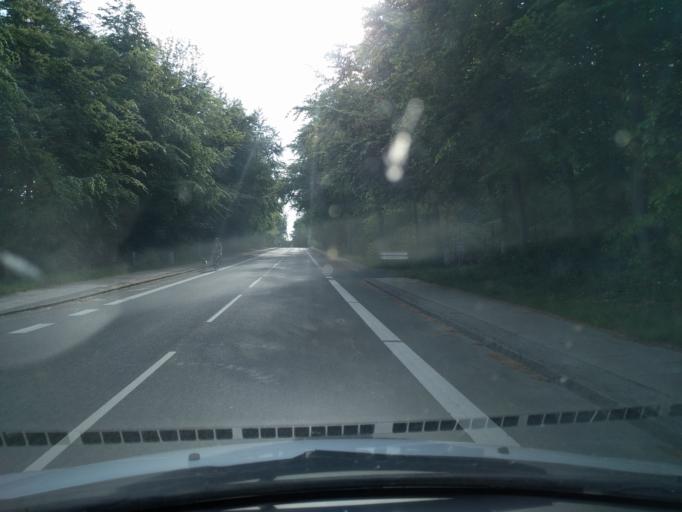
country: DK
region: South Denmark
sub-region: Nyborg Kommune
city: Nyborg
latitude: 55.3185
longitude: 10.8092
